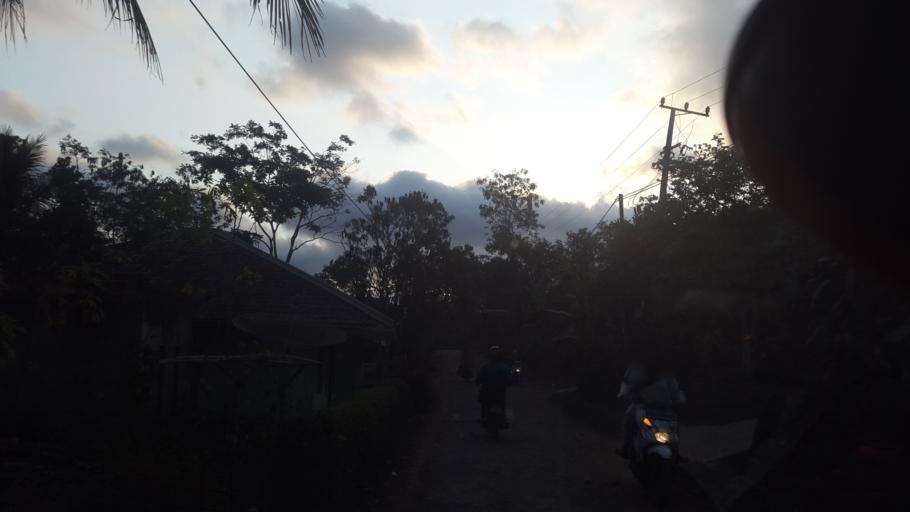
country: ID
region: West Java
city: Datarnangka
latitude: -7.2123
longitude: 106.8554
